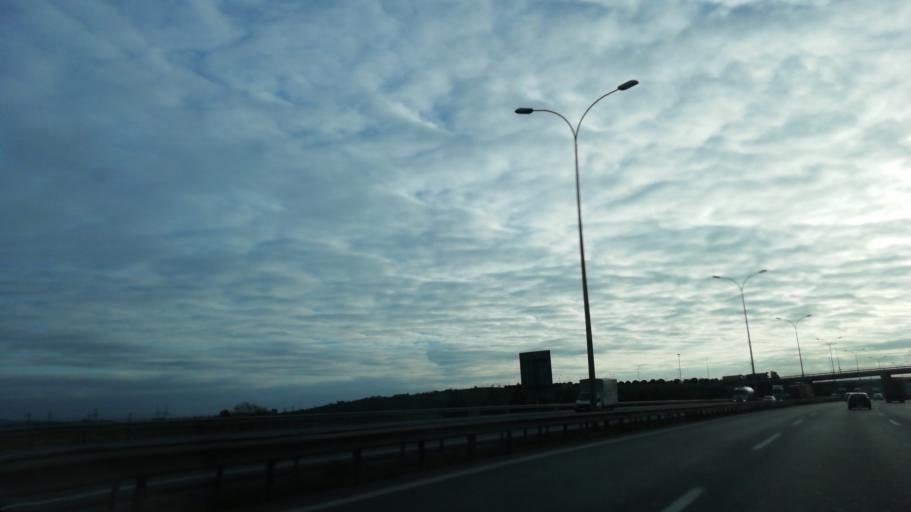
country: TR
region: Istanbul
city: Sultanbeyli
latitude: 40.9319
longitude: 29.3427
